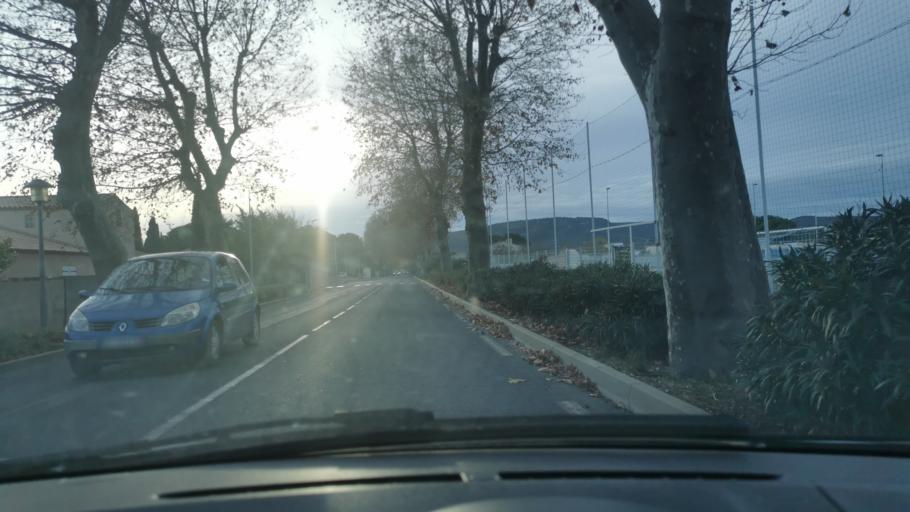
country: FR
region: Languedoc-Roussillon
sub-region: Departement de l'Herault
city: Mireval
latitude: 43.5067
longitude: 3.7972
